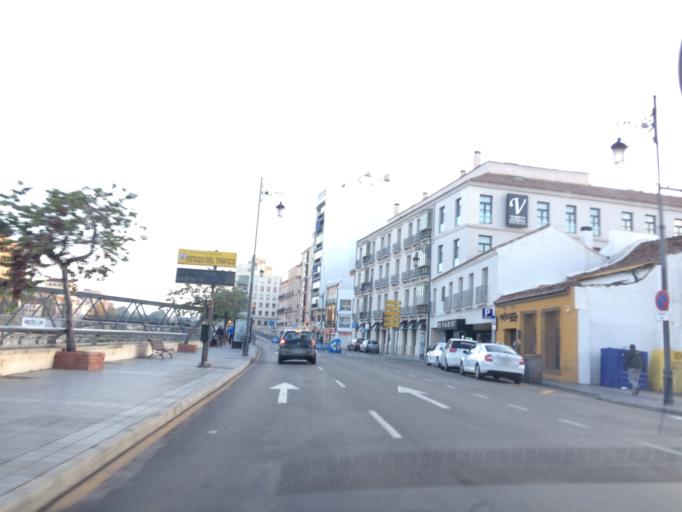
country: ES
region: Andalusia
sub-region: Provincia de Malaga
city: Malaga
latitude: 36.7197
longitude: -4.4252
